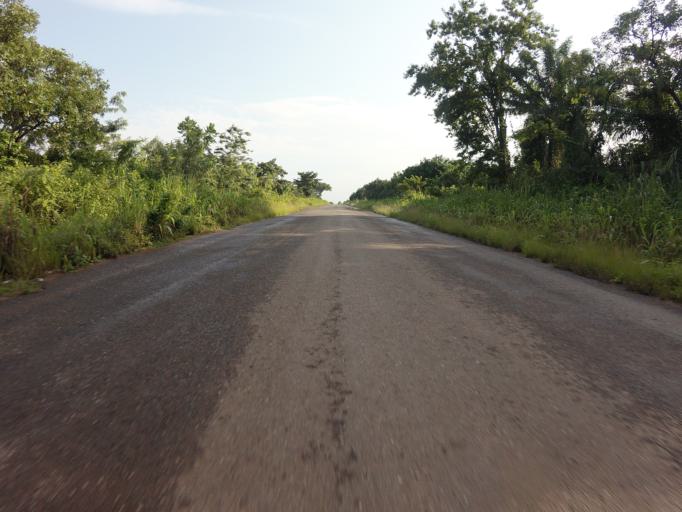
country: GH
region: Volta
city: Hohoe
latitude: 7.0807
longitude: 0.4414
